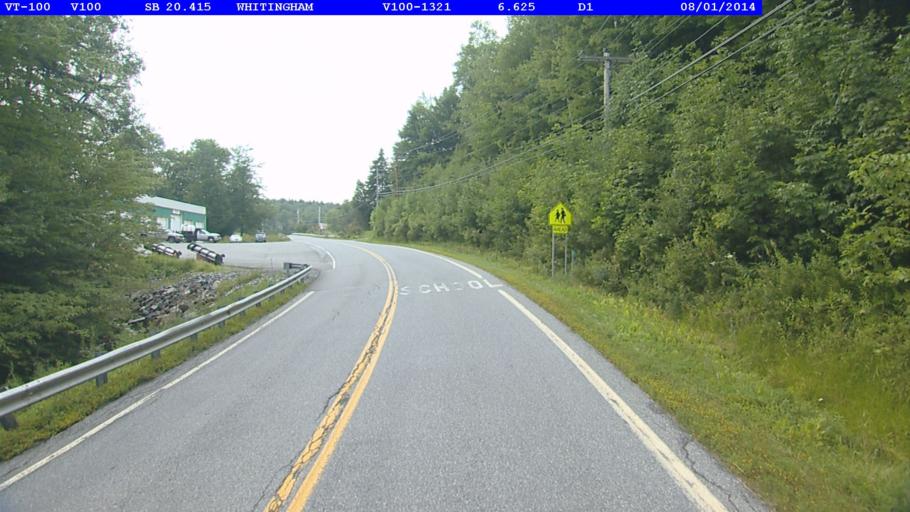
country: US
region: Vermont
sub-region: Windham County
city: Dover
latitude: 42.7889
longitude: -72.8373
